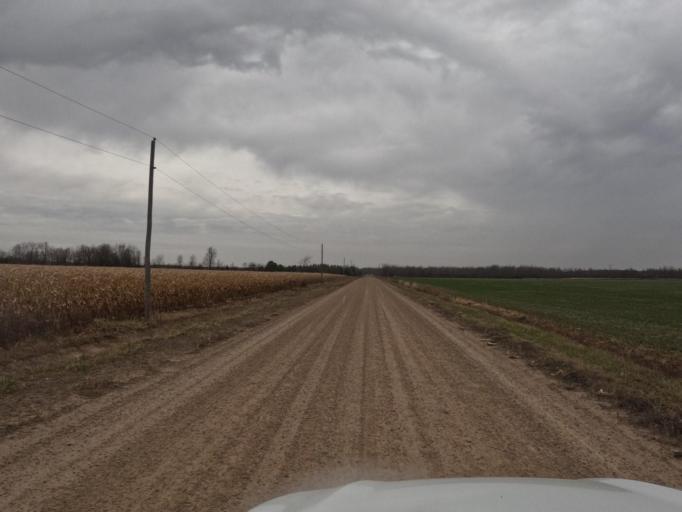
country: CA
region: Ontario
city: Shelburne
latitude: 43.8885
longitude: -80.3827
